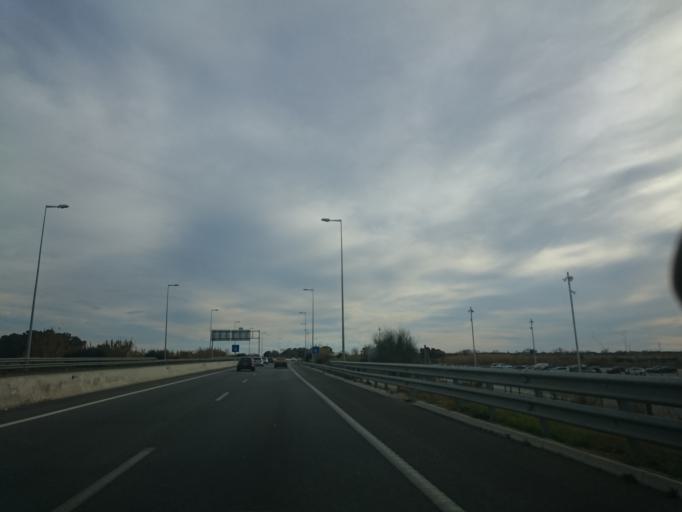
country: ES
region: Catalonia
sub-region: Provincia de Barcelona
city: Viladecans
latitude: 41.2883
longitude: 2.0519
